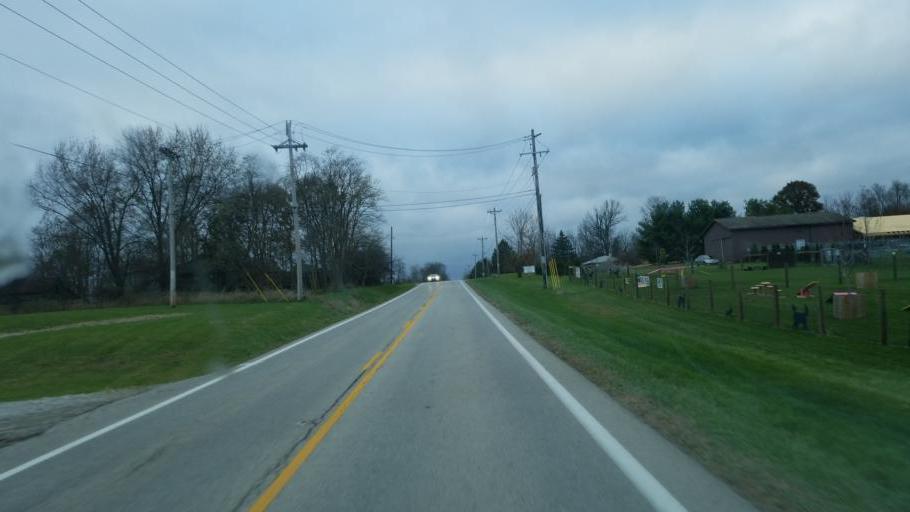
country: US
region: Ohio
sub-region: Delaware County
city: Sunbury
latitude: 40.3607
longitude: -82.8306
